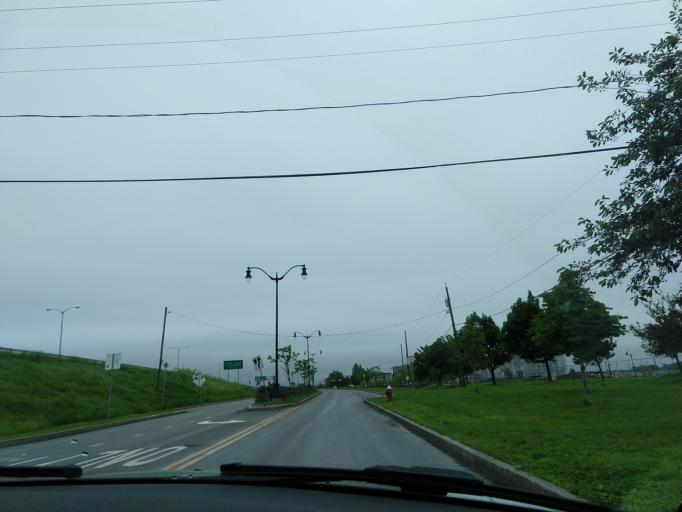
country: US
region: New York
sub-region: Erie County
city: Lackawanna
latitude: 42.8458
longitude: -78.8608
